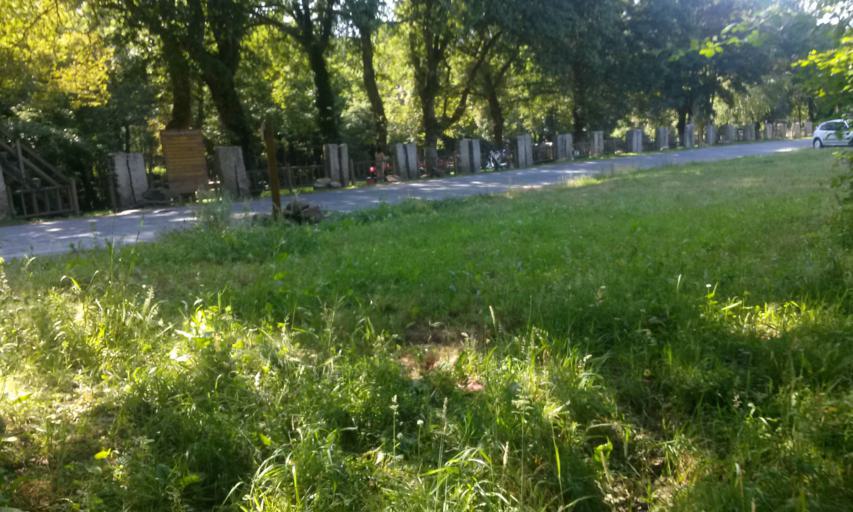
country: ES
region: Galicia
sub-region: Provincia de Lugo
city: Begonte
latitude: 43.1698
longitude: -7.7548
